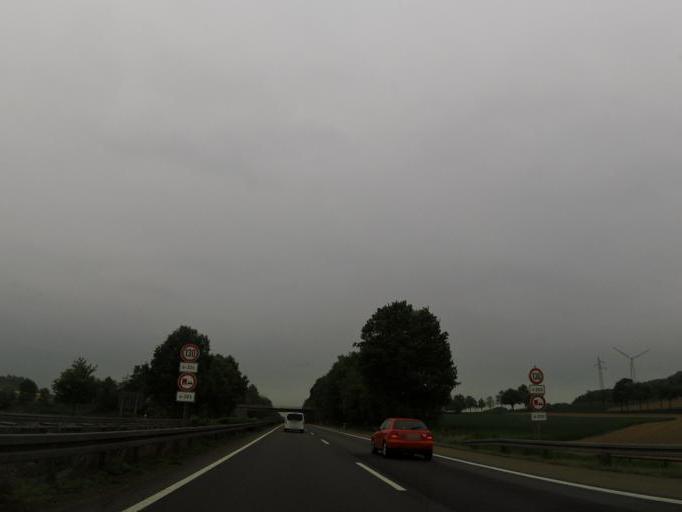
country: DE
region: Lower Saxony
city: Gittelde
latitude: 51.8298
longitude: 10.1141
